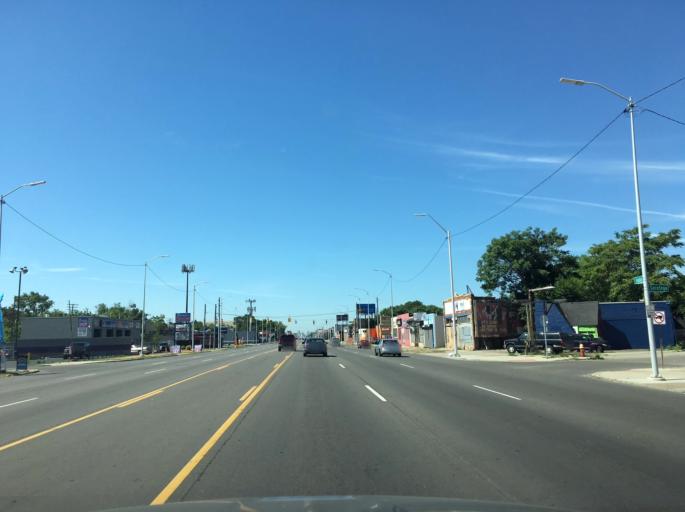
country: US
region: Michigan
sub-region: Macomb County
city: Eastpointe
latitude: 42.4326
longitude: -82.9794
